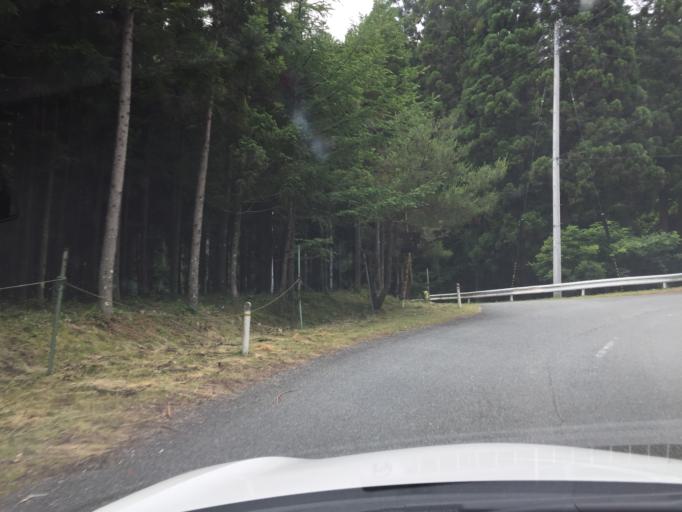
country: JP
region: Fukushima
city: Iwaki
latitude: 37.1482
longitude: 140.7003
